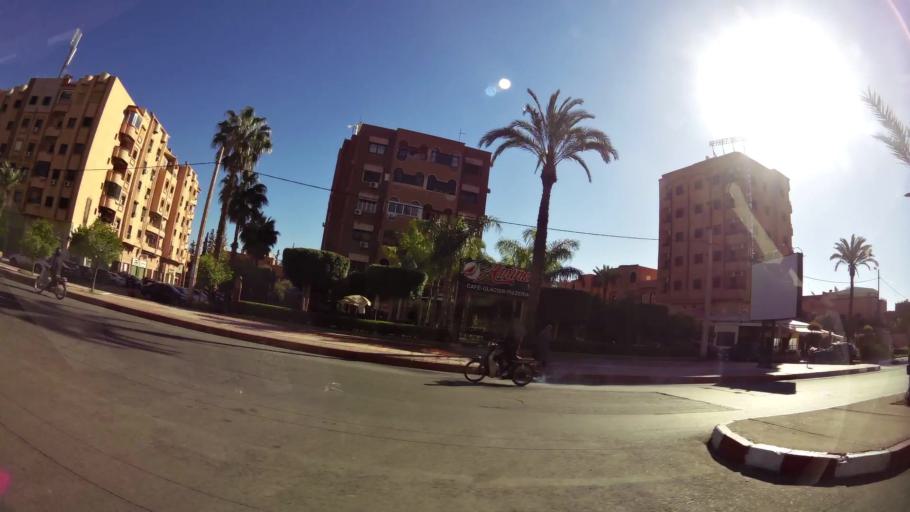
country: MA
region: Marrakech-Tensift-Al Haouz
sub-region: Marrakech
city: Marrakesh
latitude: 31.6521
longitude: -8.0168
